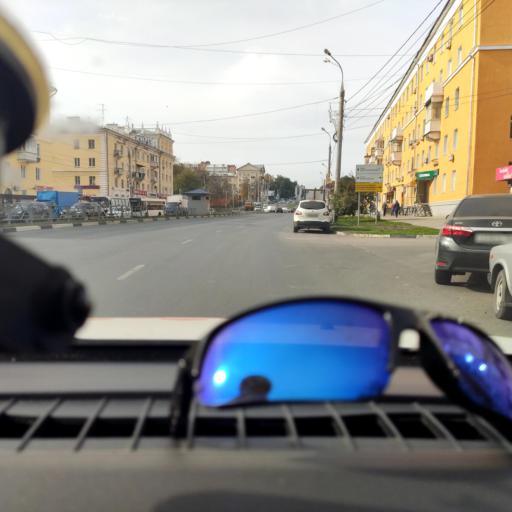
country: RU
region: Samara
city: Samara
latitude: 53.2018
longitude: 50.2235
